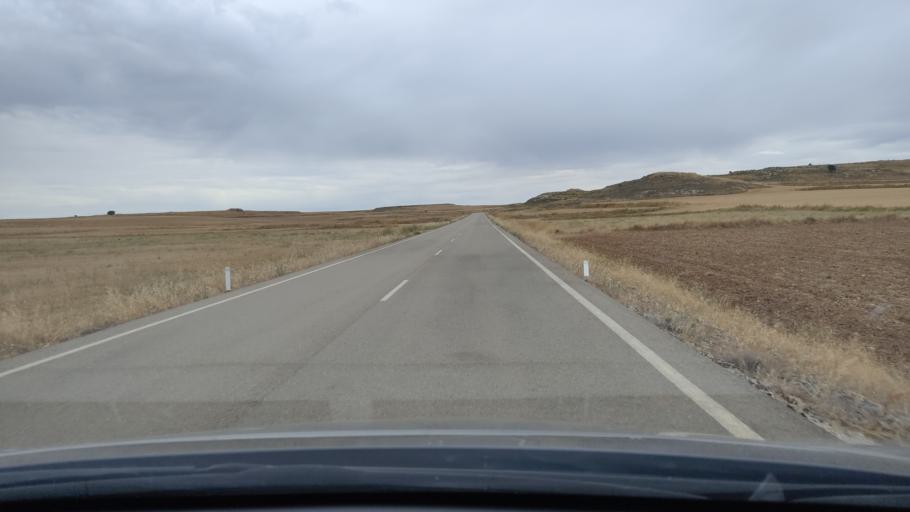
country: ES
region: Aragon
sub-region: Provincia de Zaragoza
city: Anento
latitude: 41.0486
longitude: -1.2997
